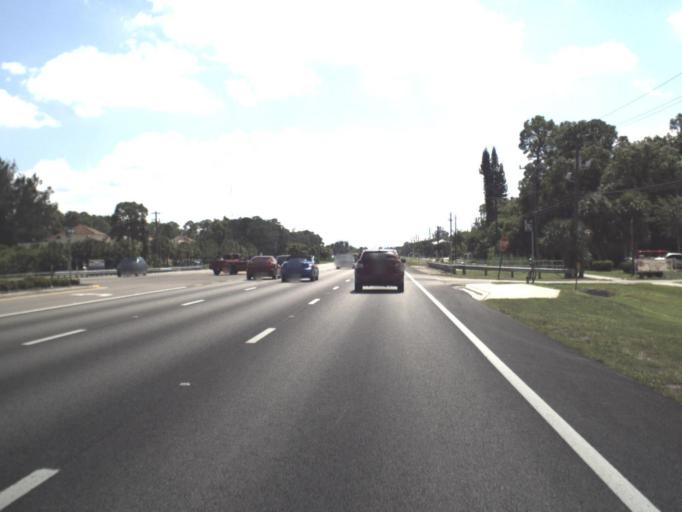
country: US
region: Florida
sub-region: Lee County
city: San Carlos Park
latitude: 26.4598
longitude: -81.8276
